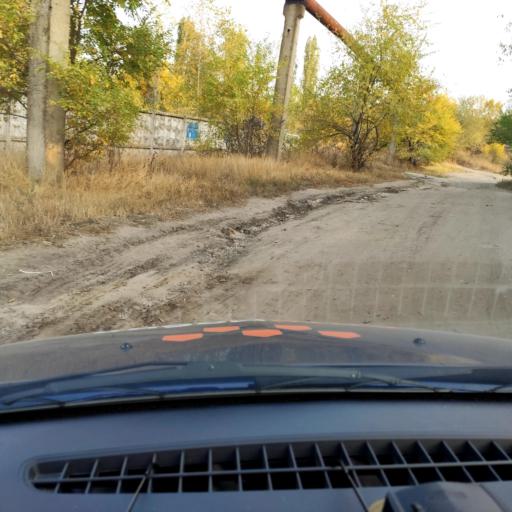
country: RU
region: Voronezj
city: Pridonskoy
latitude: 51.6648
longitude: 39.1126
